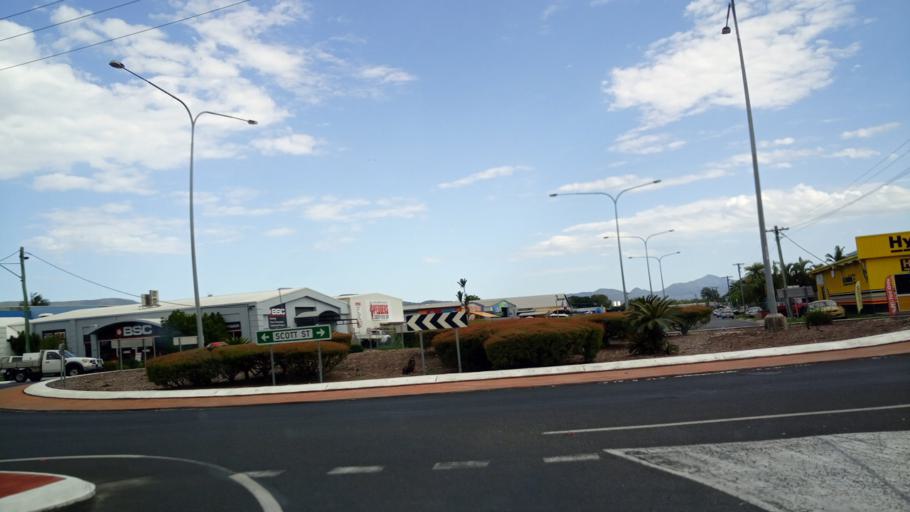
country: AU
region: Queensland
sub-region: Cairns
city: Woree
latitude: -16.9365
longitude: 145.7566
